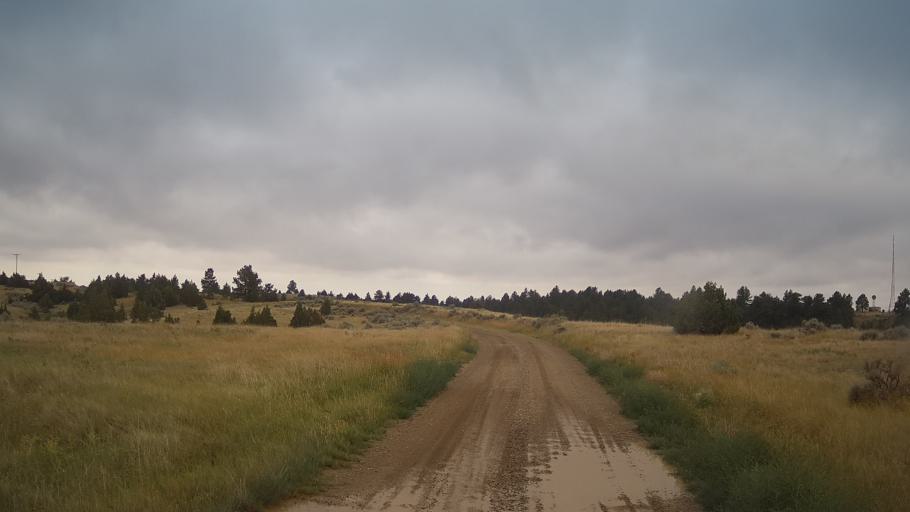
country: US
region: Montana
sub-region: Dawson County
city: Glendive
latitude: 47.0475
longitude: -104.6783
